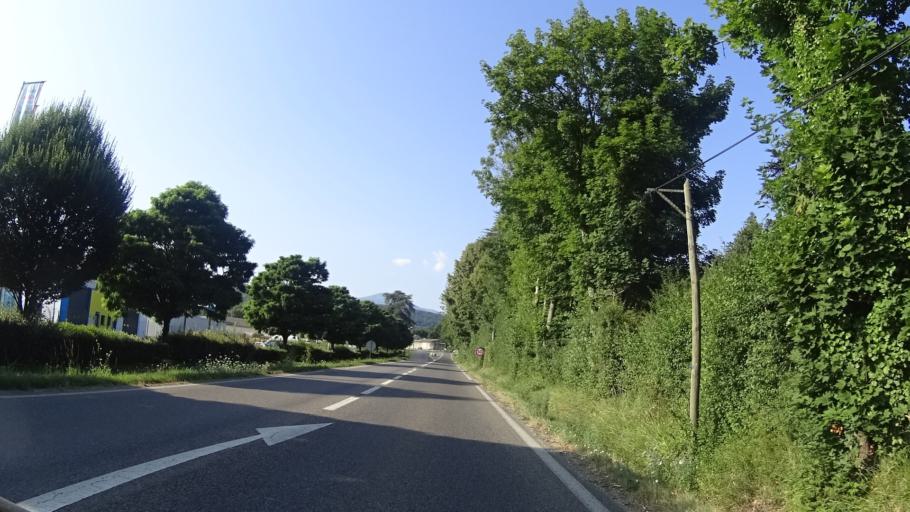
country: FR
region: Midi-Pyrenees
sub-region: Departement de l'Ariege
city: Lavelanet
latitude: 42.9520
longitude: 1.8599
